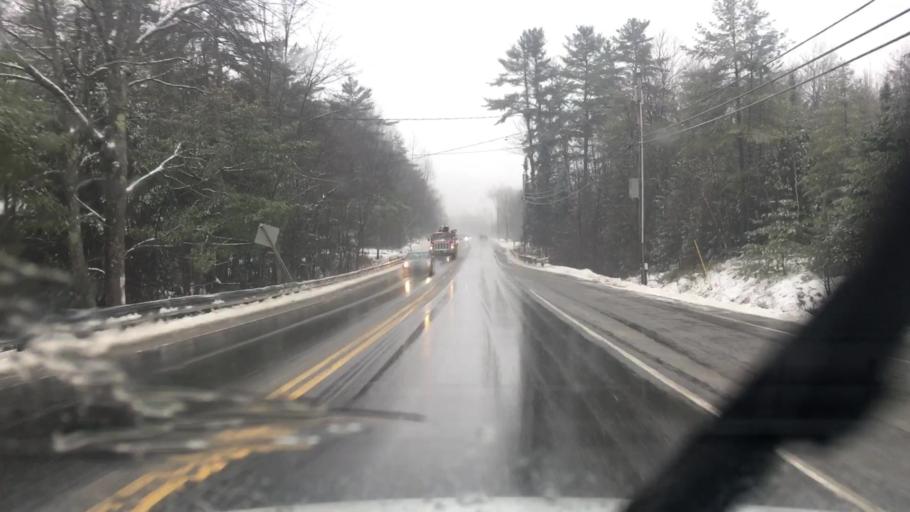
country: US
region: Maine
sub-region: Cumberland County
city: Gorham
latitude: 43.6820
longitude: -70.4721
